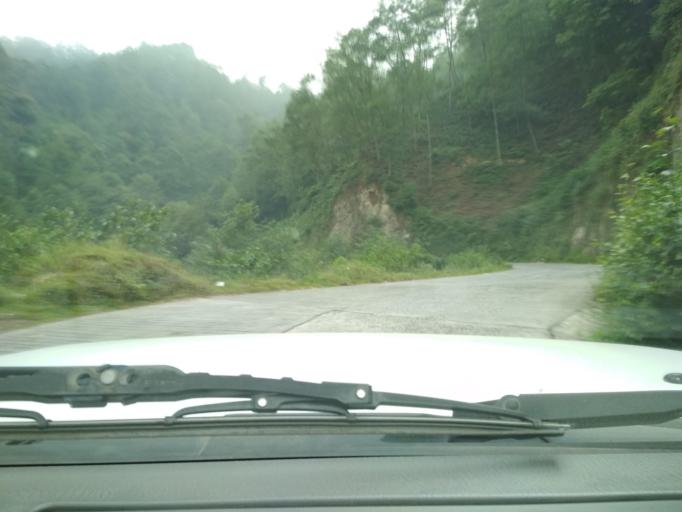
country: MX
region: Veracruz
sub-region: La Perla
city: Metlac Hernandez (Metlac Primero)
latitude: 18.9740
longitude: -97.1459
